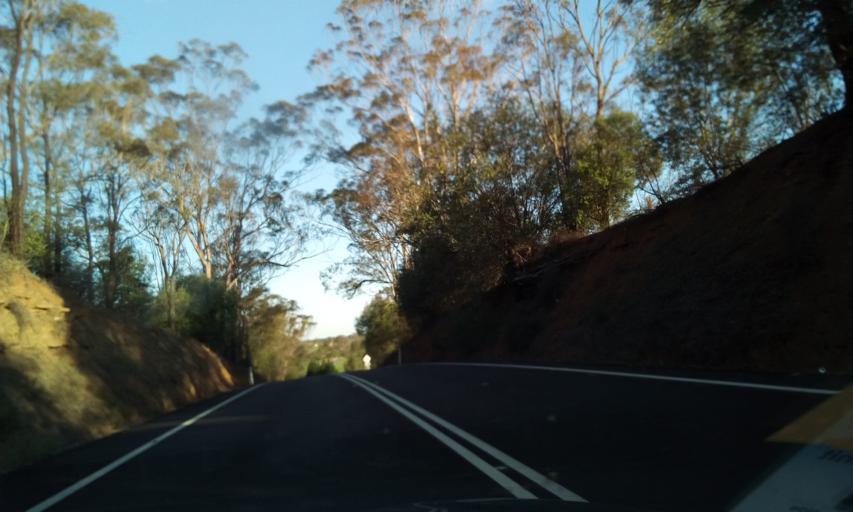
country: AU
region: New South Wales
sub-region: Camden
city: Camden South
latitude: -34.1298
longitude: 150.7052
